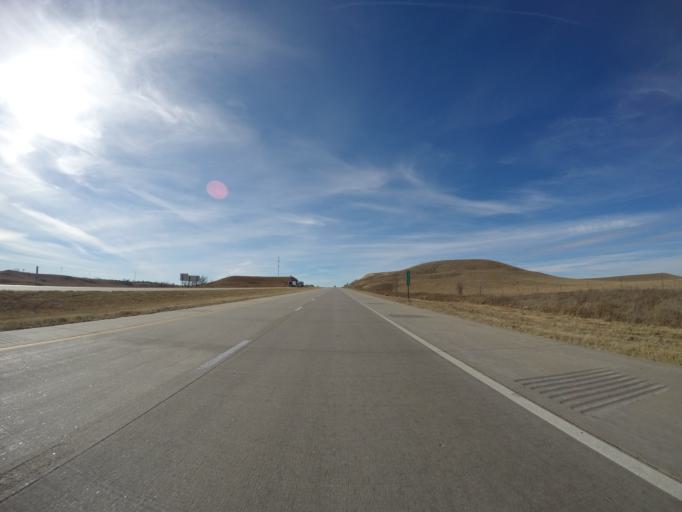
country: US
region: Kansas
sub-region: Riley County
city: Ogden
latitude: 39.0663
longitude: -96.6674
